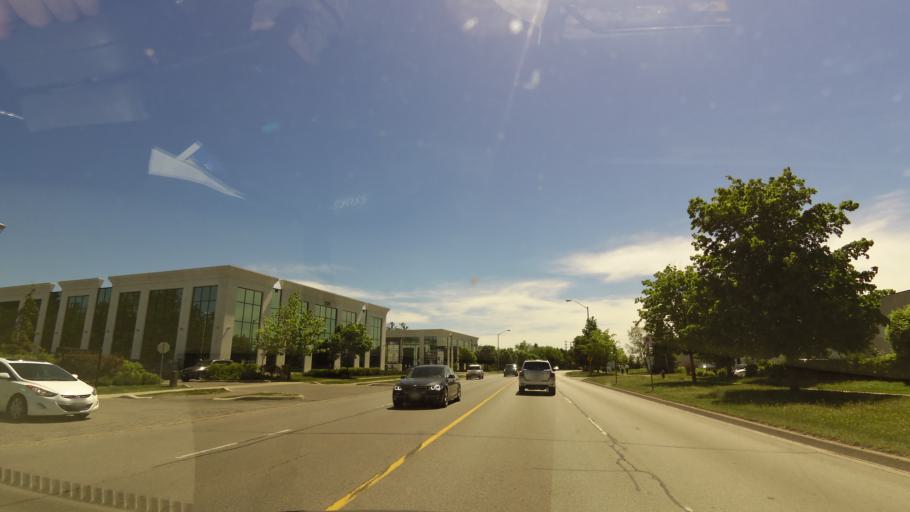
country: CA
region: Ontario
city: Oakville
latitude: 43.4737
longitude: -79.6640
